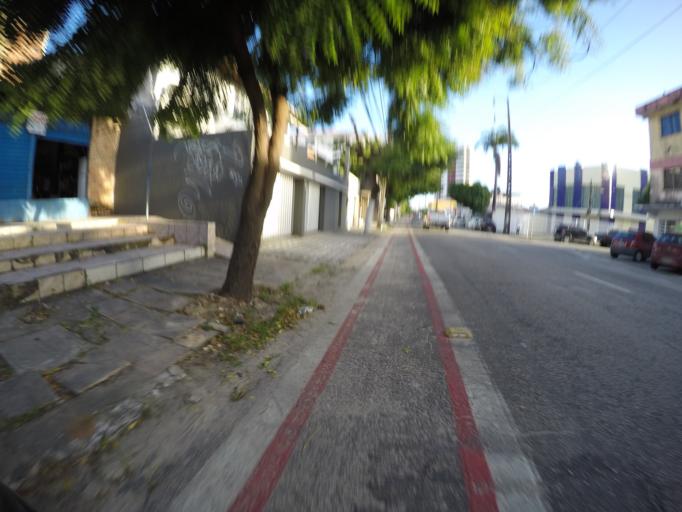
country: BR
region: Ceara
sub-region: Fortaleza
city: Fortaleza
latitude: -3.7447
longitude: -38.5122
